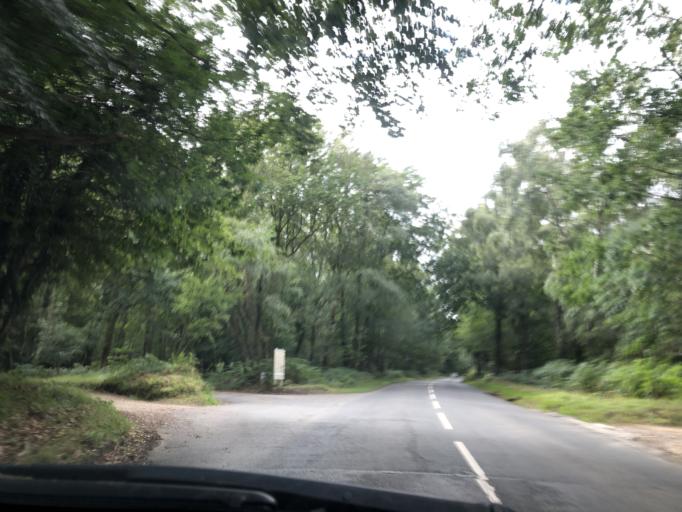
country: GB
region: England
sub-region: East Sussex
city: Forest Row
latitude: 51.0792
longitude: 0.0681
